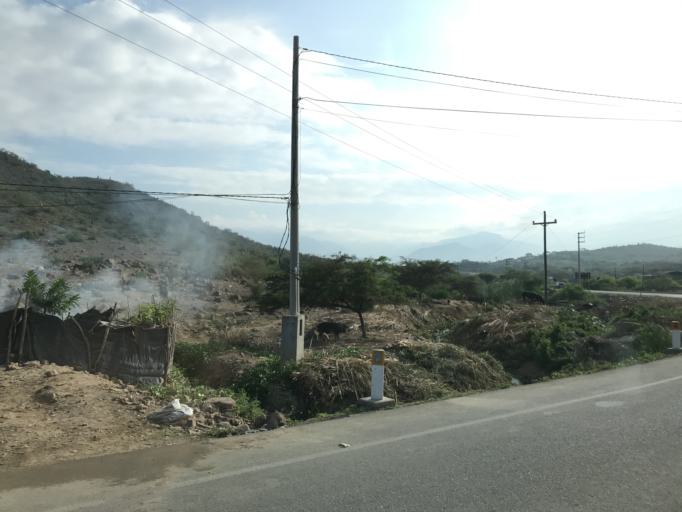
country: PE
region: Lambayeque
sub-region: Provincia de Chiclayo
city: Chongoyape
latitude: -6.6330
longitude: -79.3892
